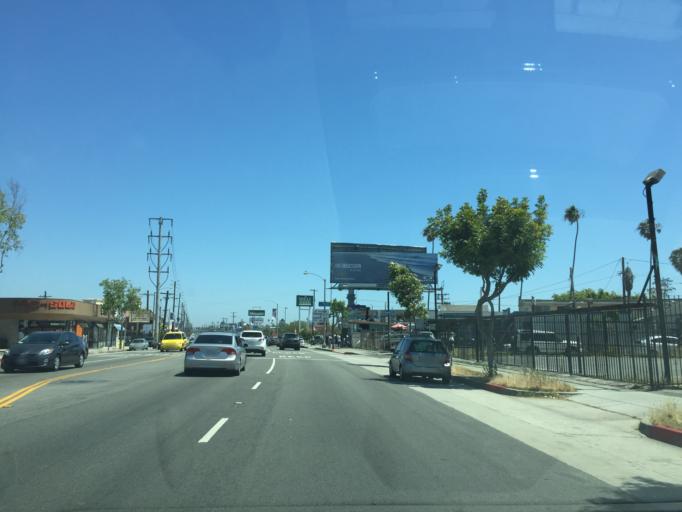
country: US
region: California
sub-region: Los Angeles County
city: Santa Monica
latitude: 34.0030
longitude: -118.4711
